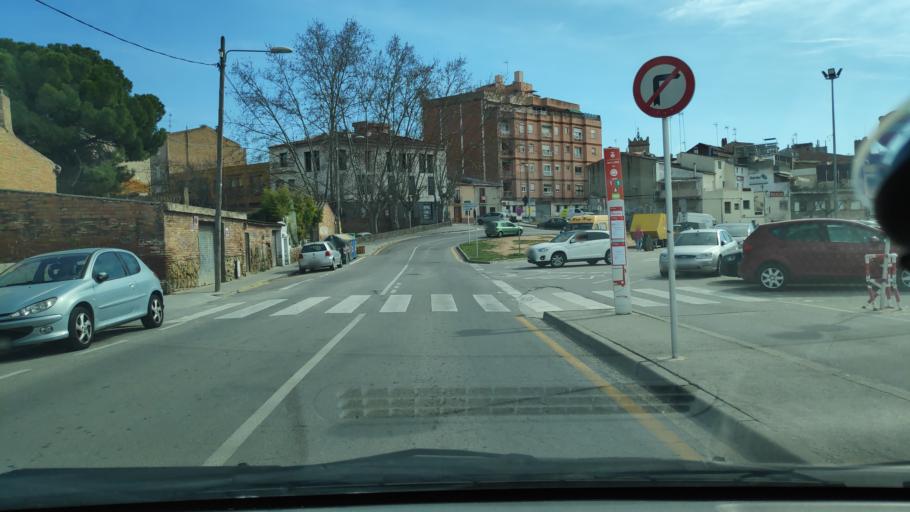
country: ES
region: Catalonia
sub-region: Provincia de Barcelona
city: Rubi
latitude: 41.4934
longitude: 2.0295
